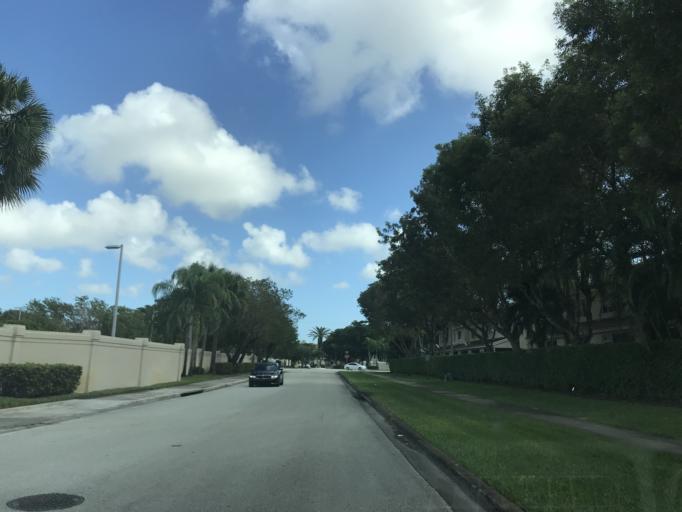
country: US
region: Florida
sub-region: Broward County
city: Coconut Creek
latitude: 26.2710
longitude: -80.1958
